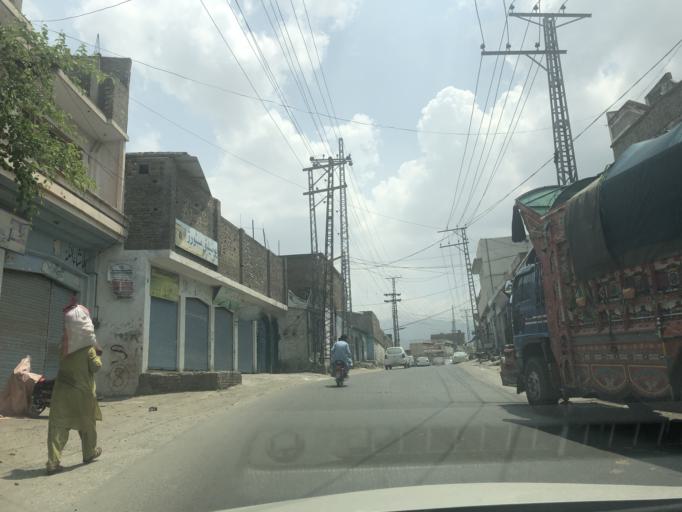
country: PK
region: Khyber Pakhtunkhwa
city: Mingora
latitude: 34.7717
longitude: 72.3494
